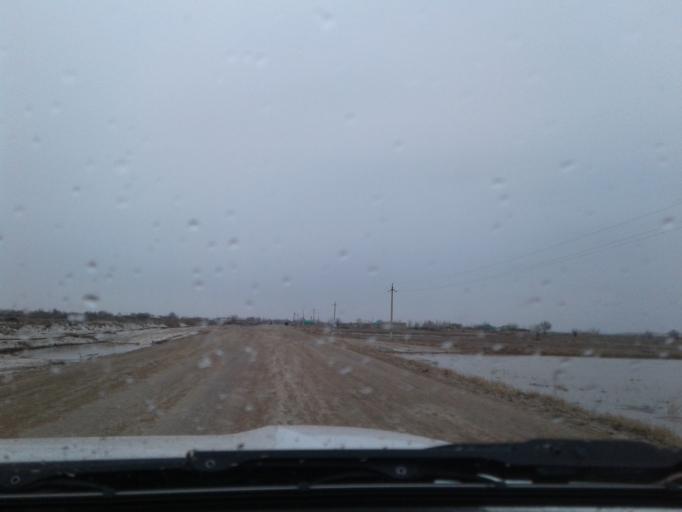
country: UZ
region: Karakalpakstan
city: Shumanay Shahri
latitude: 42.2805
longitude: 58.6436
